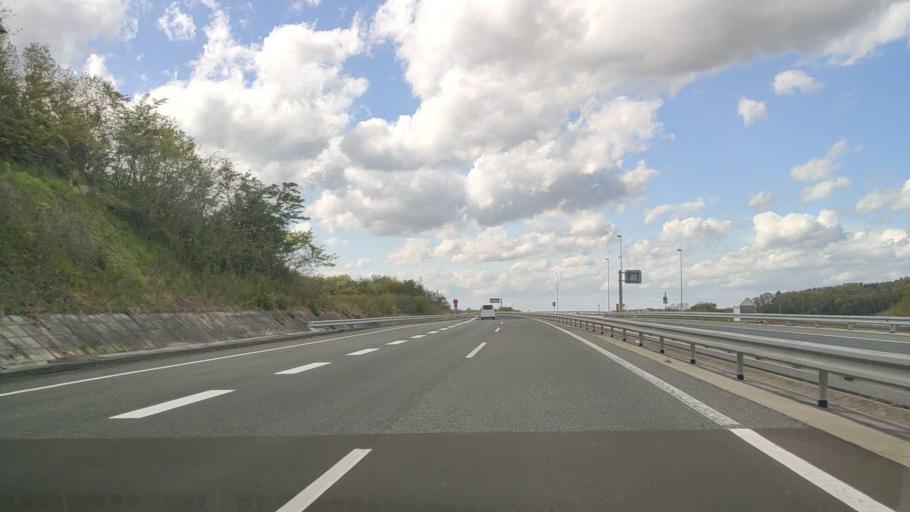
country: JP
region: Miyagi
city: Rifu
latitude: 38.3533
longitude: 140.9536
